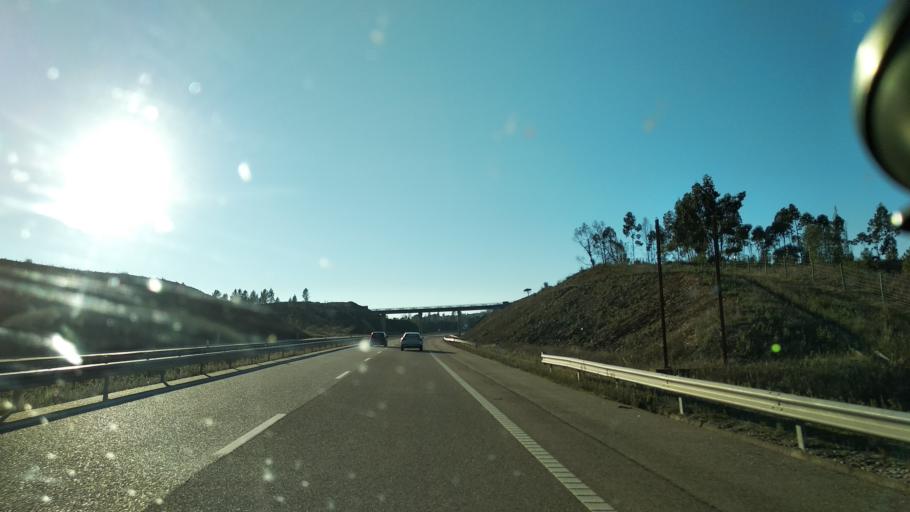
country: PT
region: Santarem
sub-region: Macao
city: Macao
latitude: 39.4936
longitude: -8.0561
